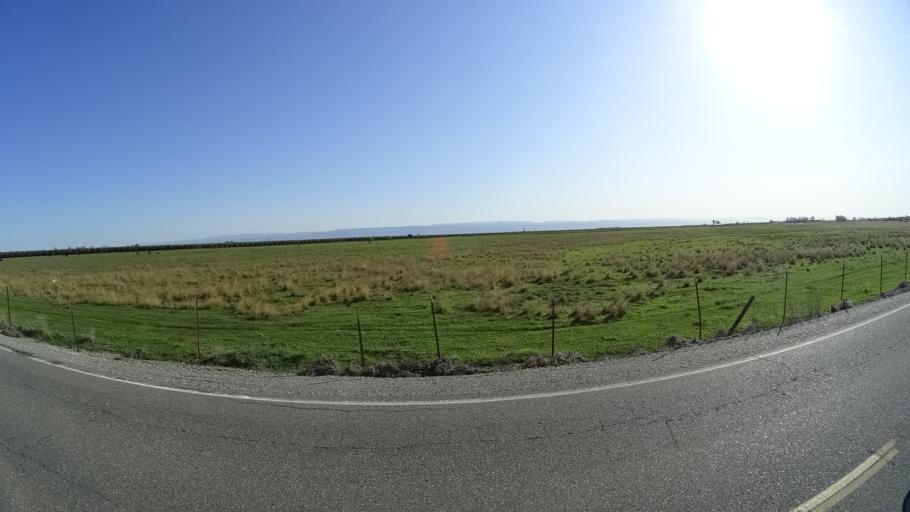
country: US
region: California
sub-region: Glenn County
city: Hamilton City
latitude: 39.7483
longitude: -122.0990
